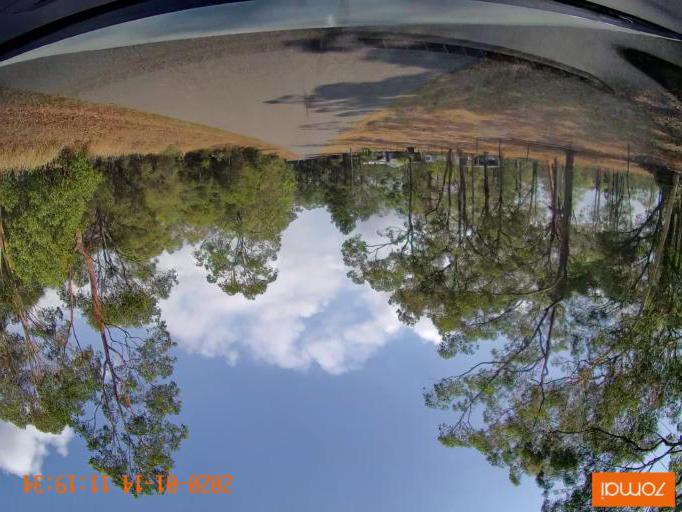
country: AU
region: New South Wales
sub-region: Lake Macquarie Shire
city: Cooranbong
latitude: -33.0985
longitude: 151.4602
